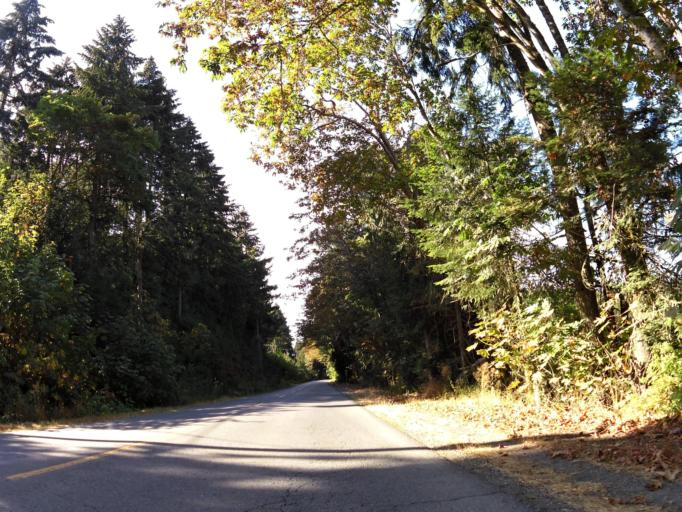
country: CA
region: British Columbia
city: North Saanich
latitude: 48.6915
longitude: -123.5598
